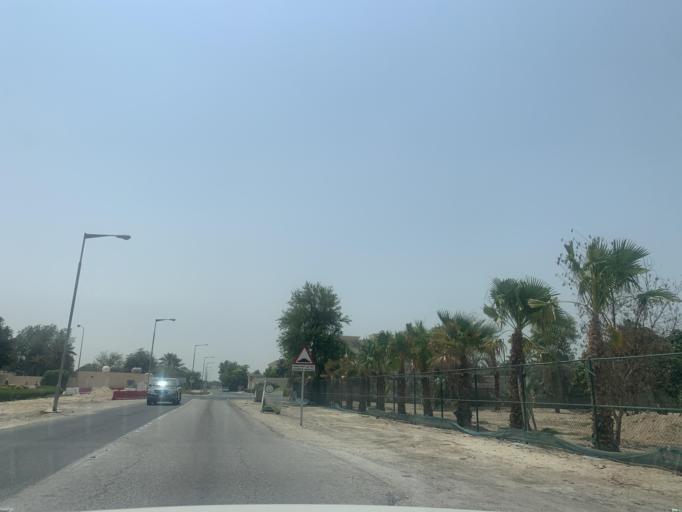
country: BH
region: Central Governorate
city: Madinat Hamad
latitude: 26.1504
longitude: 50.4649
